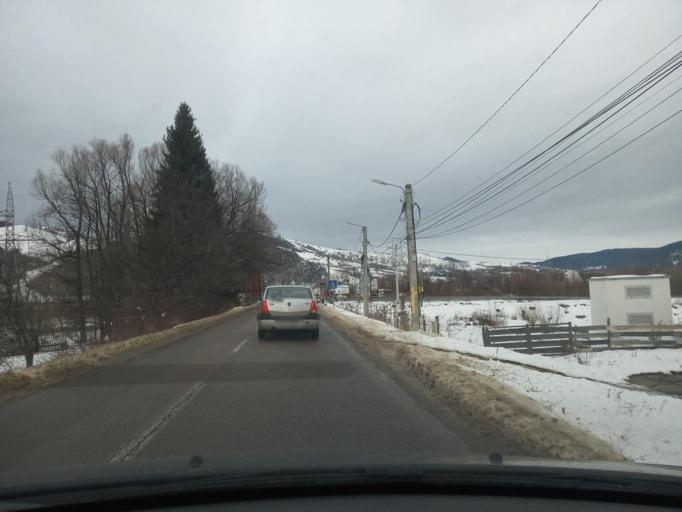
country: RO
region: Suceava
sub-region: Oras Gura Humorului
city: Gura Humorului
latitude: 47.5376
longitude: 25.8645
